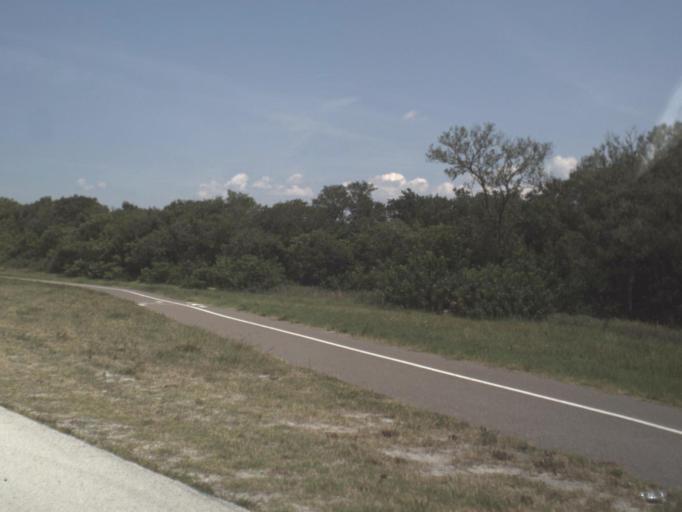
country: US
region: Florida
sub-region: Pinellas County
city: Tierra Verde
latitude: 27.6581
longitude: -82.7197
